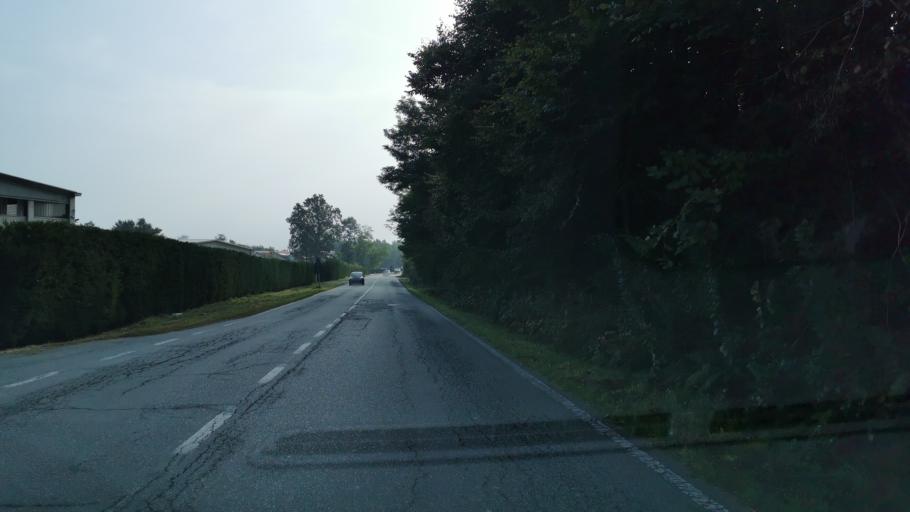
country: IT
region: Piedmont
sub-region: Provincia di Torino
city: Front
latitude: 45.2718
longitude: 7.6740
